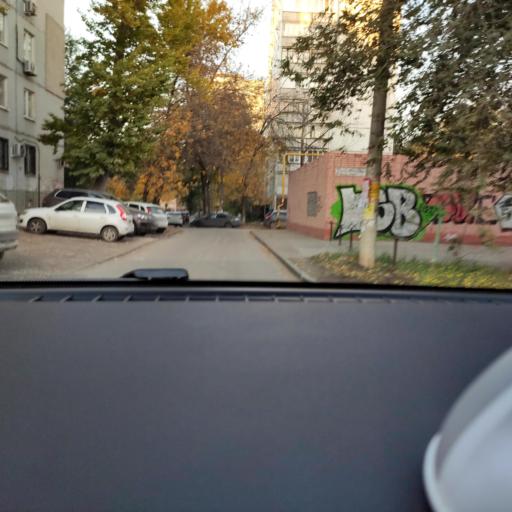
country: RU
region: Samara
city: Samara
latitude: 53.2404
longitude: 50.2139
